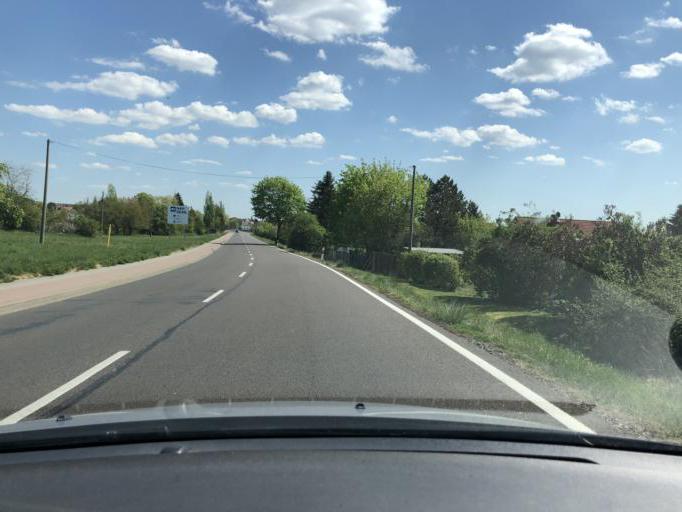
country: DE
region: Saxony
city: Schkeuditz
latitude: 51.3960
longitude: 12.1957
